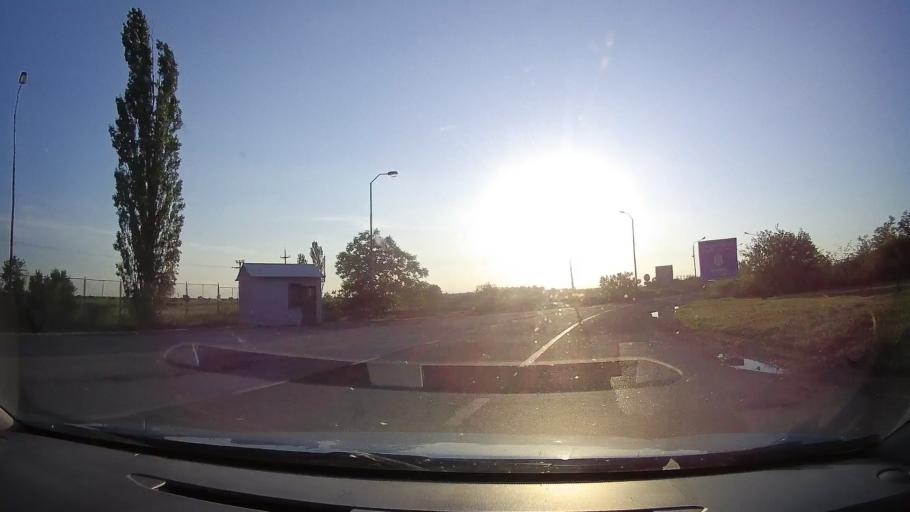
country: RO
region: Timis
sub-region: Comuna Moravita
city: Moravita
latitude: 45.2293
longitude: 21.2756
